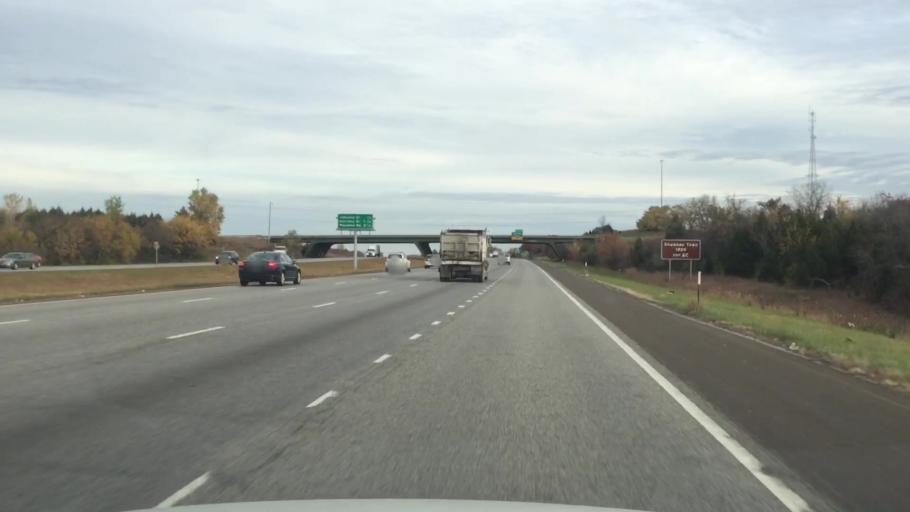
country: US
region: Kansas
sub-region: Wyandotte County
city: Edwardsville
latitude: 39.0186
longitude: -94.7847
